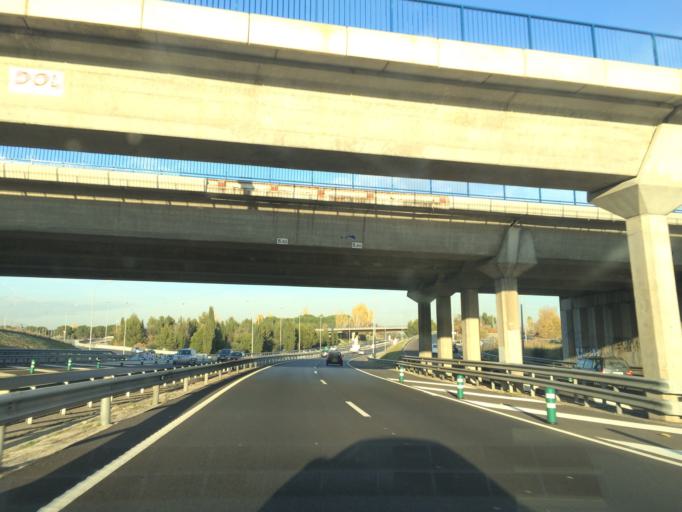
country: ES
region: Madrid
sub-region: Provincia de Madrid
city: Las Tablas
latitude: 40.5088
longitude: -3.6900
